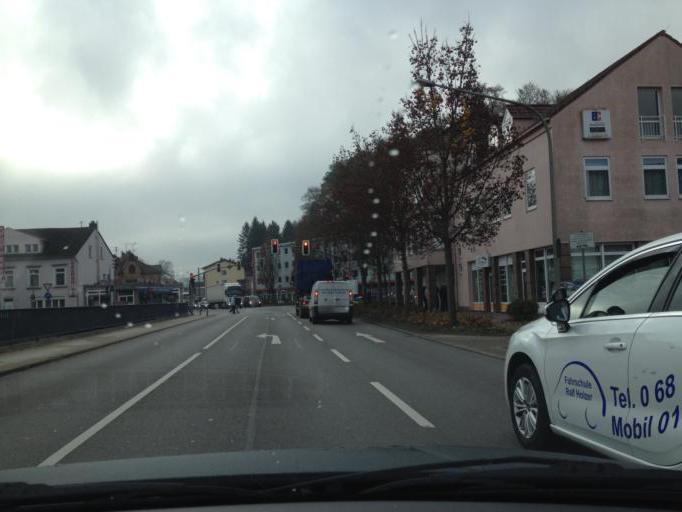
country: DE
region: Saarland
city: Ottweiler
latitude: 49.4018
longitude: 7.1639
